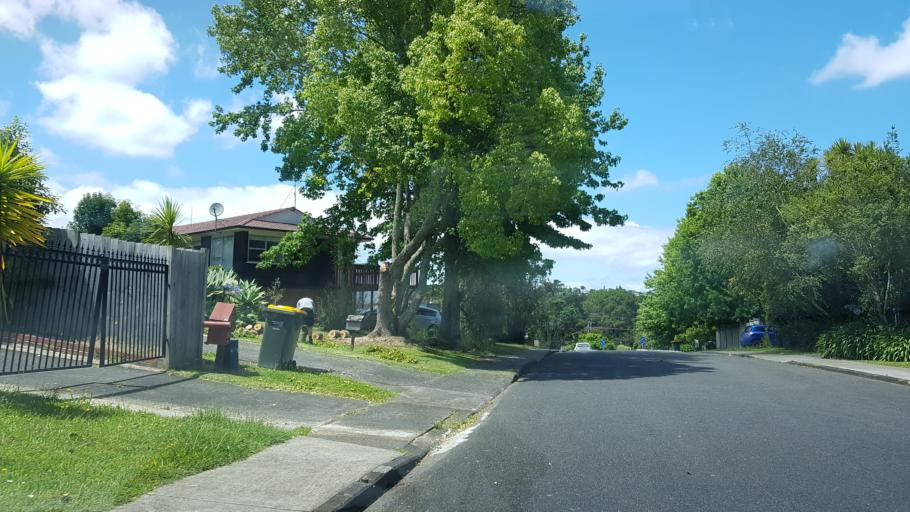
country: NZ
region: Auckland
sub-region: Auckland
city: North Shore
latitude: -36.7767
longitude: 174.7163
